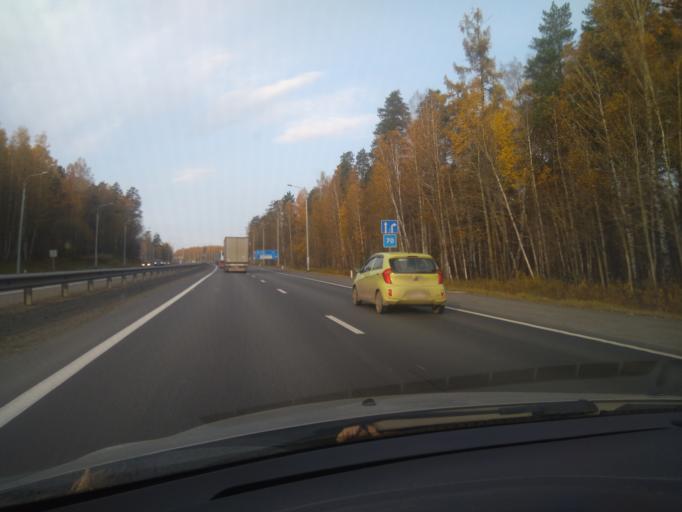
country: RU
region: Sverdlovsk
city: Talitsa
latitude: 56.8485
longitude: 60.0696
